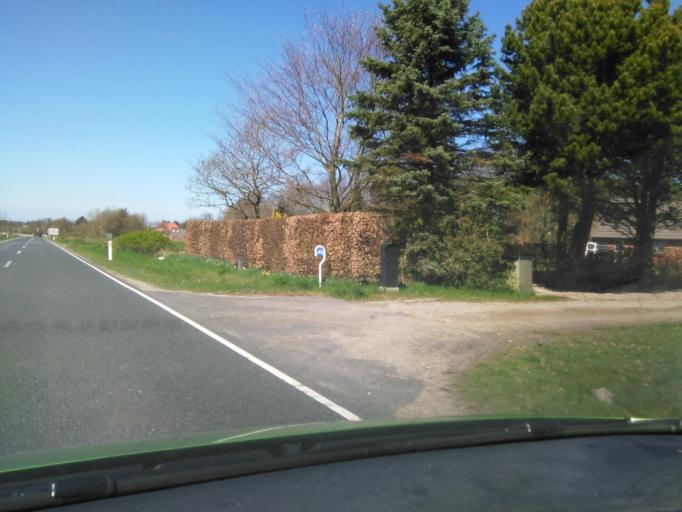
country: DK
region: South Denmark
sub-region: Billund Kommune
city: Grindsted
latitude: 55.6966
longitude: 8.9808
